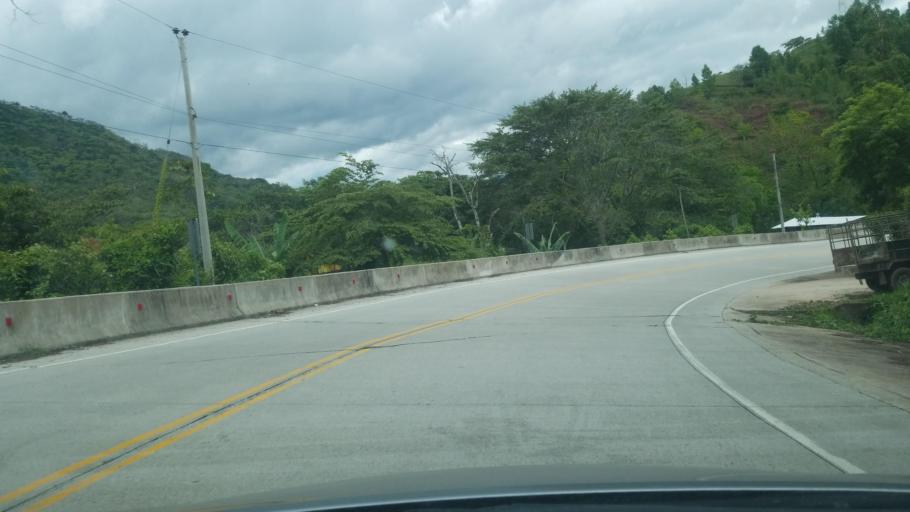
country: HN
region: Copan
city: San Jeronimo
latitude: 14.9317
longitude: -88.9523
